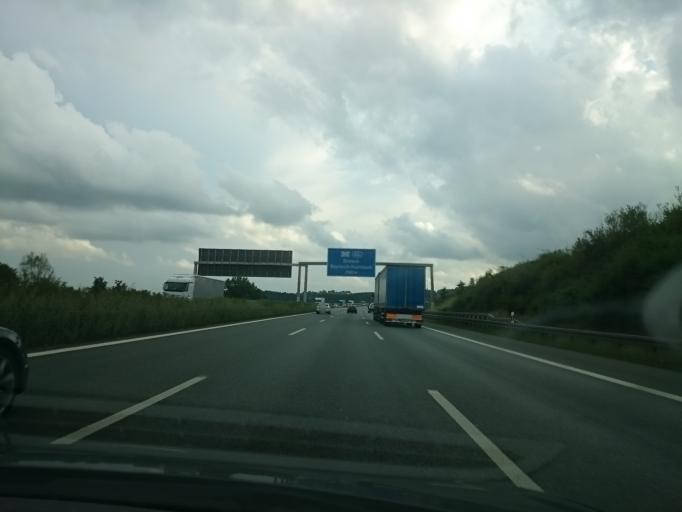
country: DE
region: Bavaria
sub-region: Upper Franconia
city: Himmelkron
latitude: 50.0488
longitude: 11.6169
